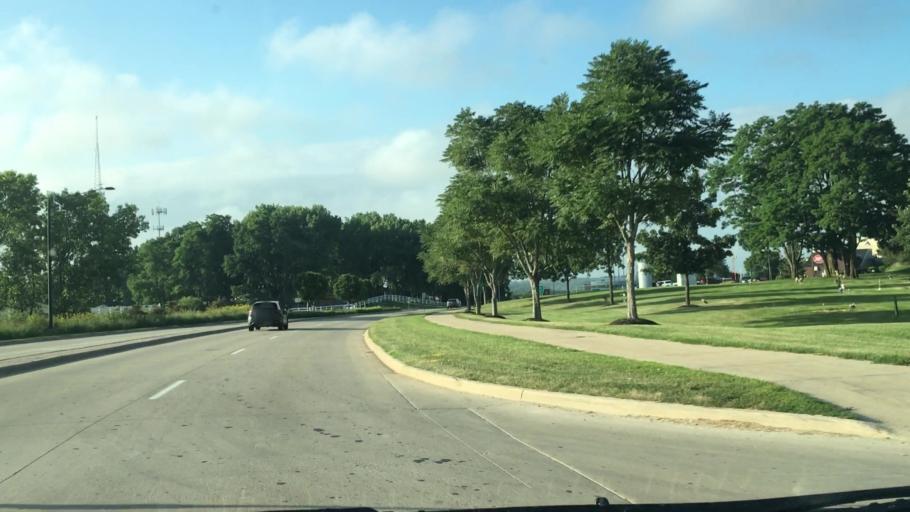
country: US
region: Iowa
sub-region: Johnson County
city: Coralville
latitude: 41.6900
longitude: -91.5647
